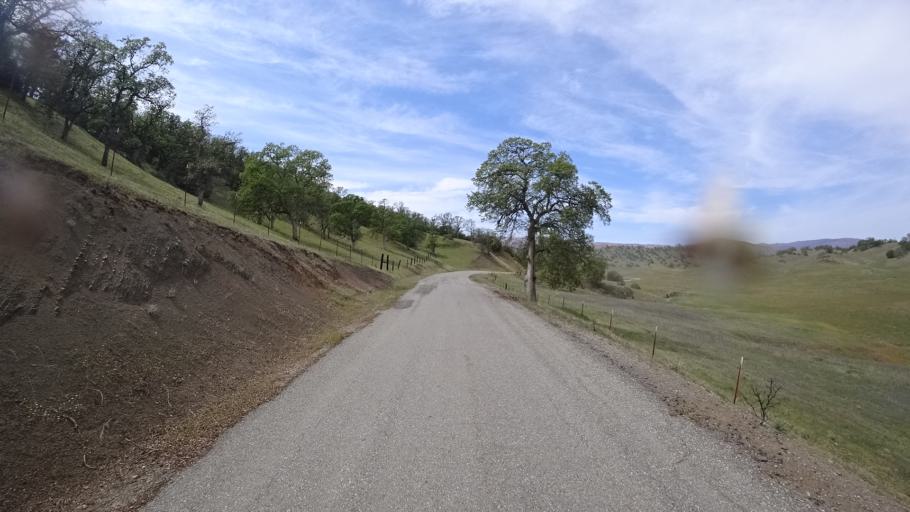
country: US
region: California
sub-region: Glenn County
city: Willows
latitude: 39.6108
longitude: -122.5636
